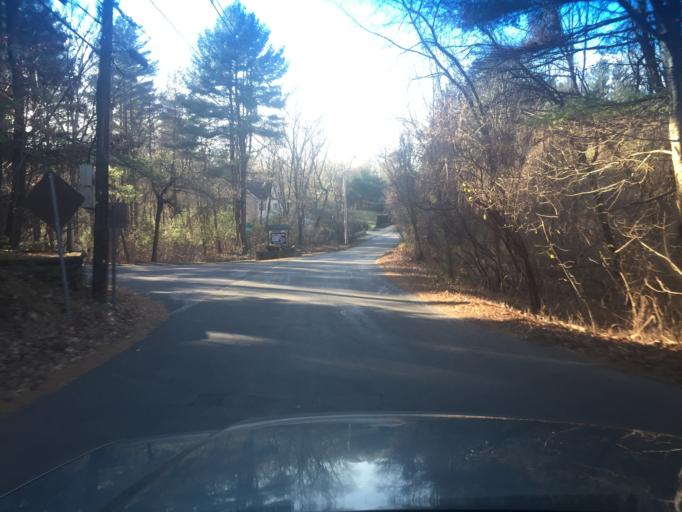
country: US
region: Massachusetts
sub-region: Middlesex County
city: Ashland
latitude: 42.2241
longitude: -71.4712
